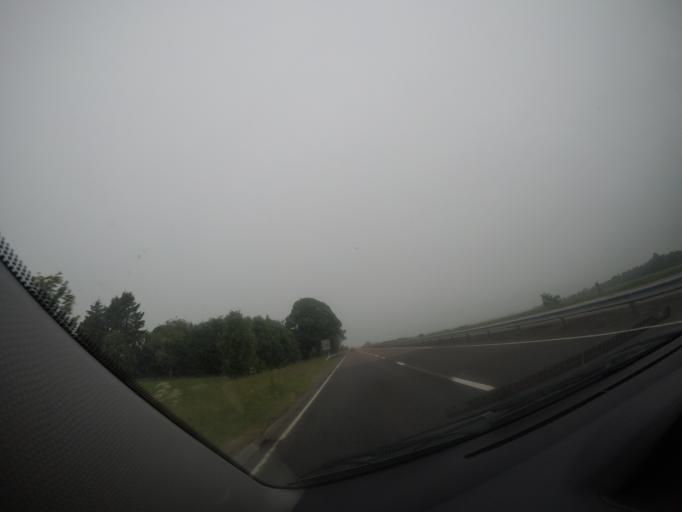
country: GB
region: Scotland
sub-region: Angus
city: Forfar
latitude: 56.5611
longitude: -2.9224
